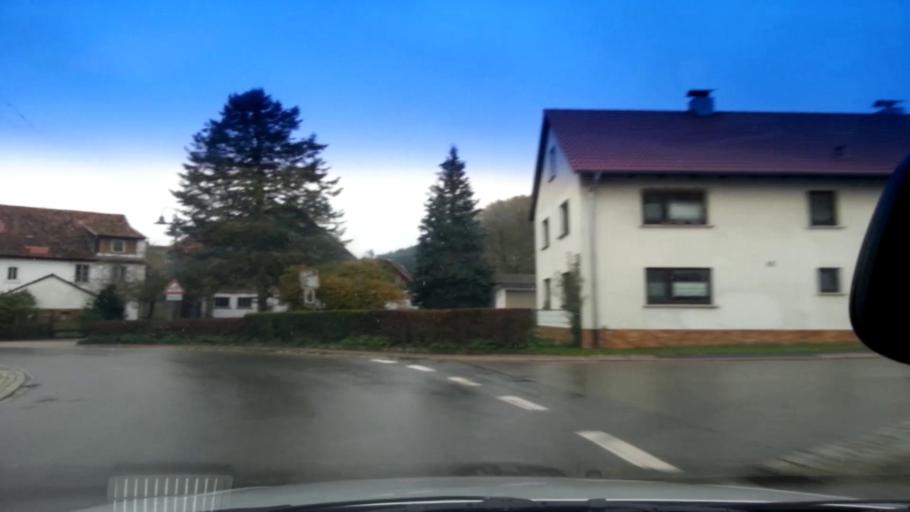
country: DE
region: Bavaria
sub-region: Upper Franconia
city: Schesslitz
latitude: 50.0120
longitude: 11.0735
